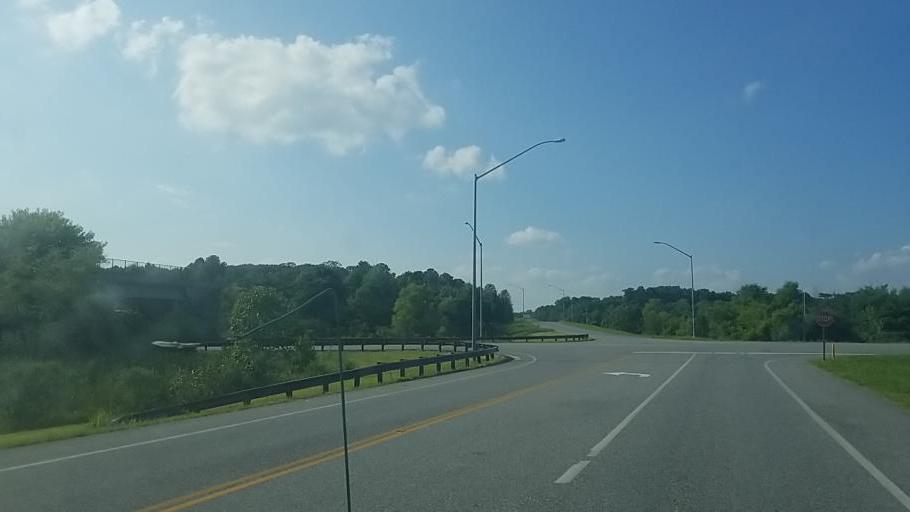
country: US
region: Maryland
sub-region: Worcester County
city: Ocean Pines
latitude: 38.3903
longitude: -75.2024
